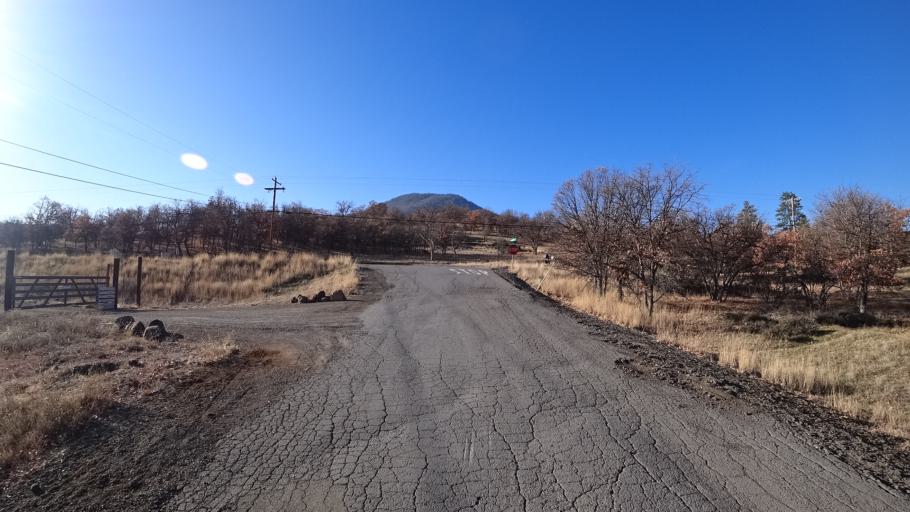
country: US
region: California
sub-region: Siskiyou County
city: Montague
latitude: 41.8897
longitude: -122.4951
